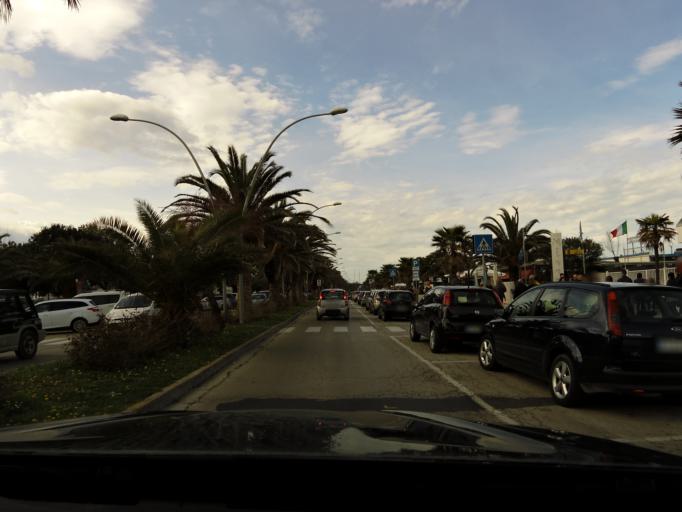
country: IT
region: The Marches
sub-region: Provincia di Macerata
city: Portocivitanova
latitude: 43.3053
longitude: 13.7351
